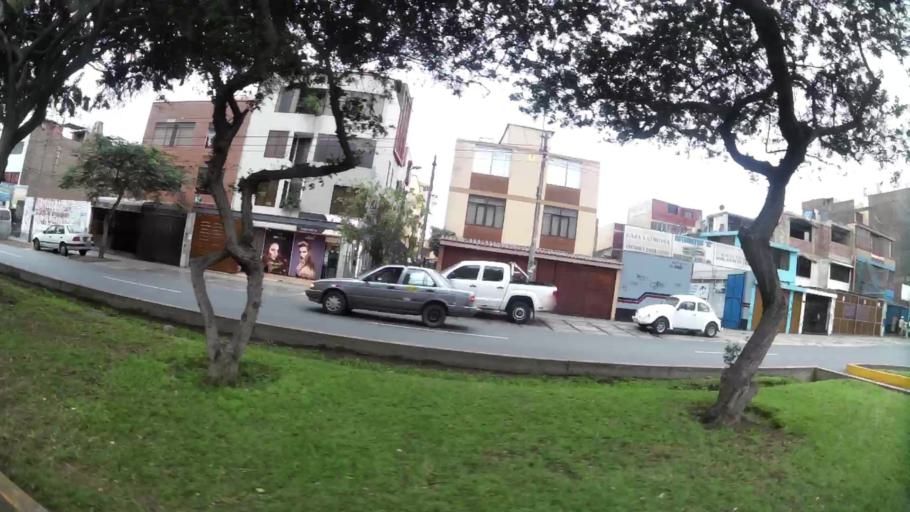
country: PE
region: Lima
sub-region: Lima
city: Surco
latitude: -12.1464
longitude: -76.9856
